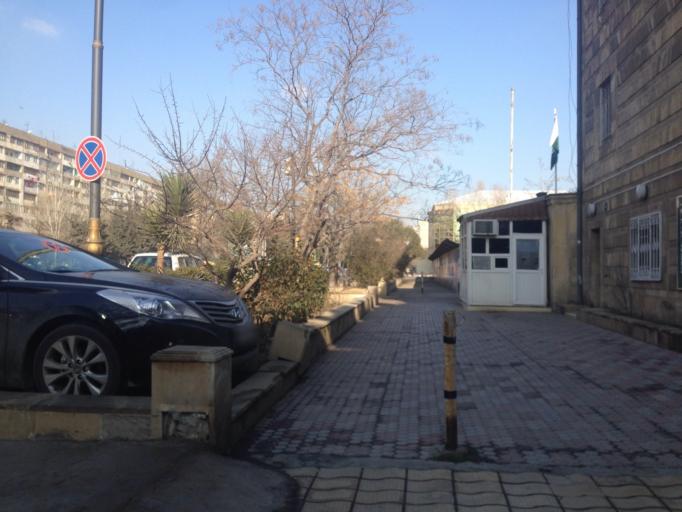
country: AZ
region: Baki
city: Baku
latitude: 40.4088
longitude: 49.8486
